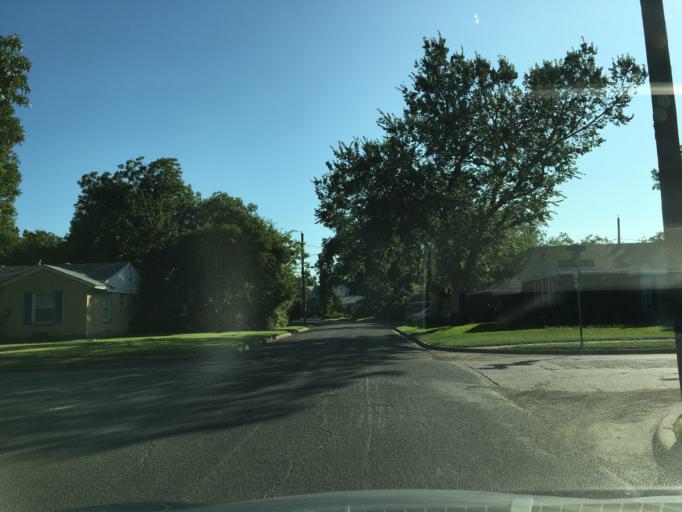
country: US
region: Texas
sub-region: Dallas County
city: Highland Park
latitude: 32.8547
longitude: -96.7087
